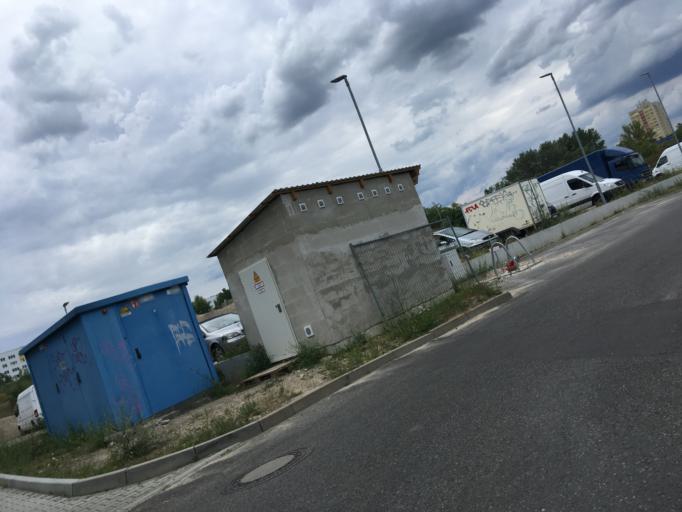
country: DE
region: Berlin
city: Fennpfuhl
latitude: 52.5294
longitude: 13.4878
